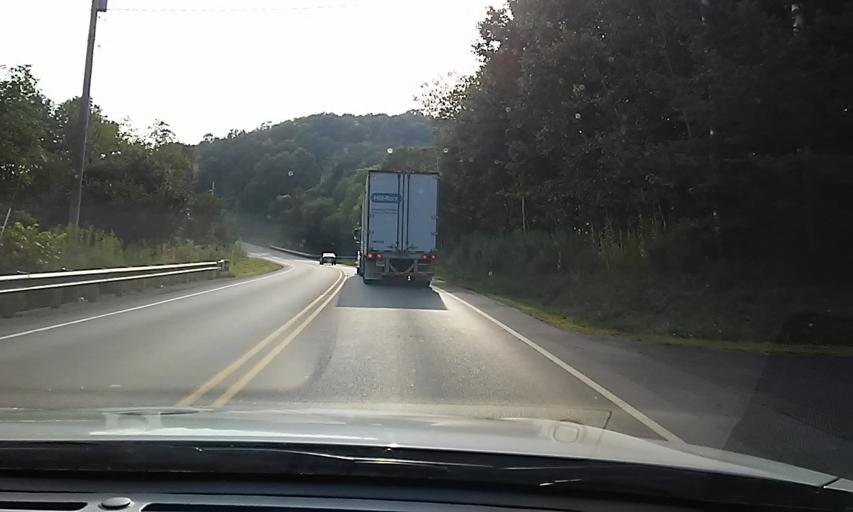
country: US
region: Pennsylvania
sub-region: McKean County
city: Port Allegany
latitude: 41.8283
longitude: -78.3366
